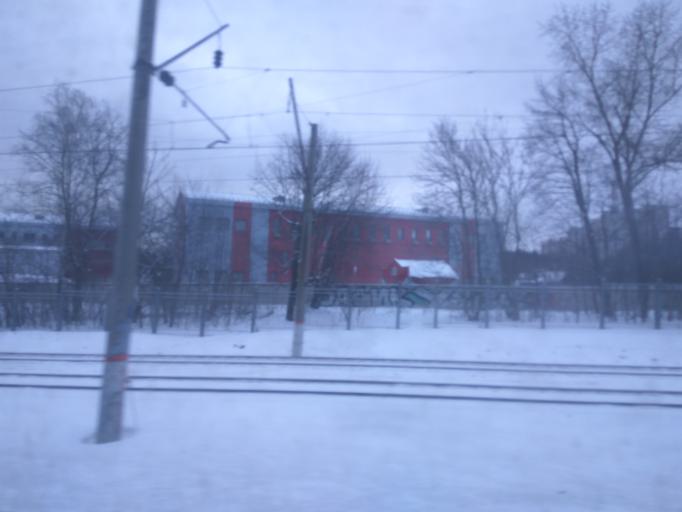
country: RU
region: Moscow
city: Annino
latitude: 55.5539
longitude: 37.5841
